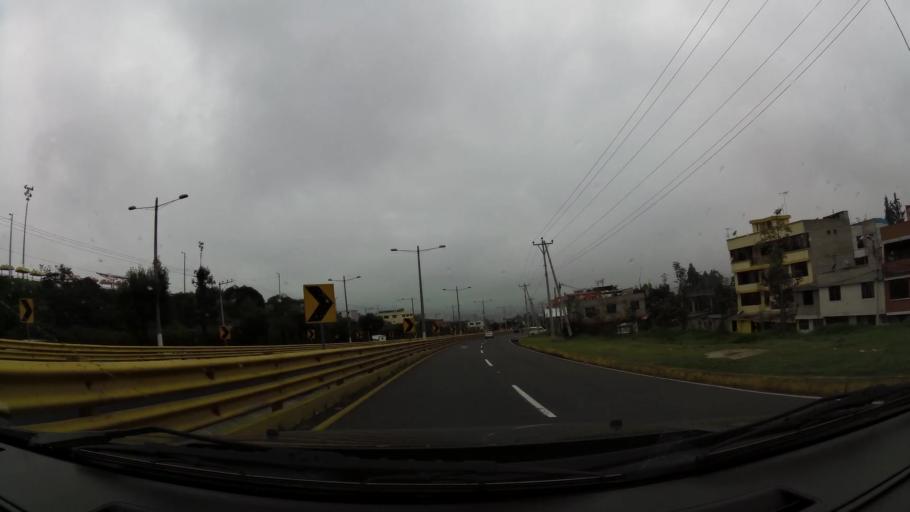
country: EC
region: Pichincha
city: Sangolqui
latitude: -0.2799
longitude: -78.4736
